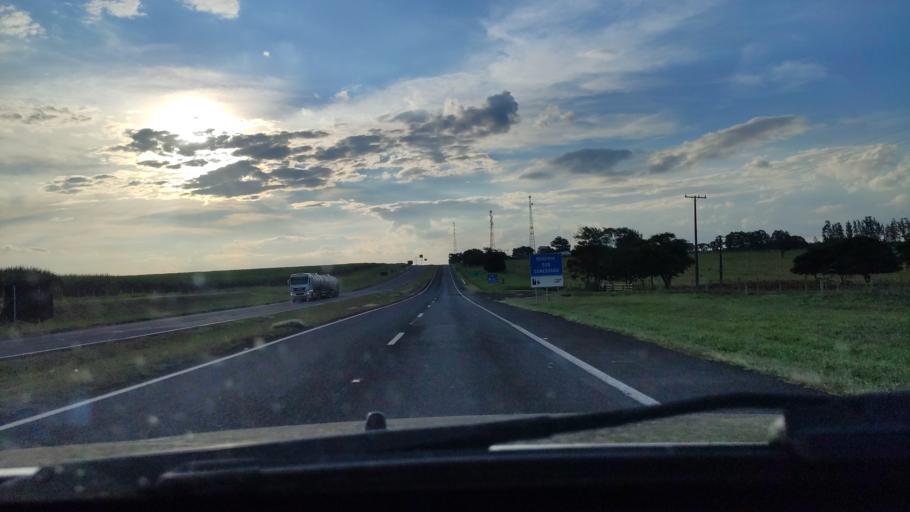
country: BR
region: Sao Paulo
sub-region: Rancharia
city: Rancharia
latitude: -22.4328
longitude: -51.0118
